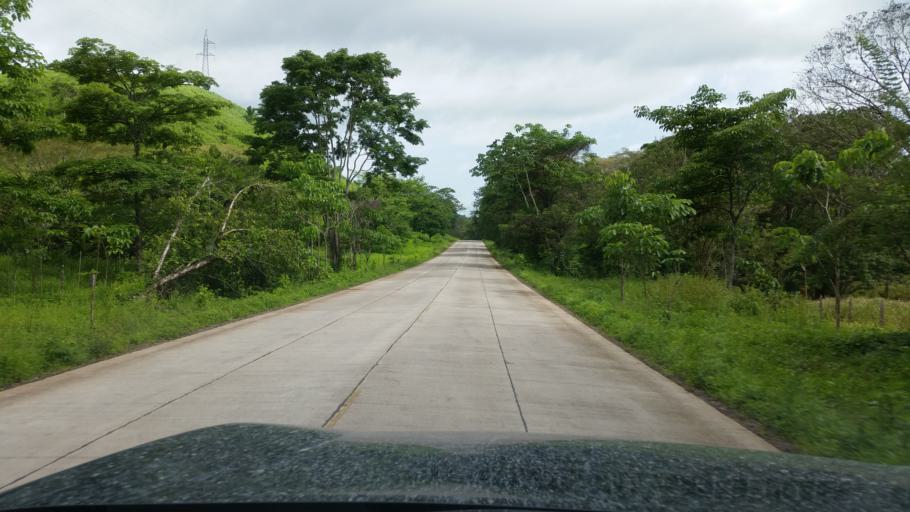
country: NI
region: Atlantico Norte (RAAN)
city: Siuna
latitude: 13.5426
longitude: -84.8236
